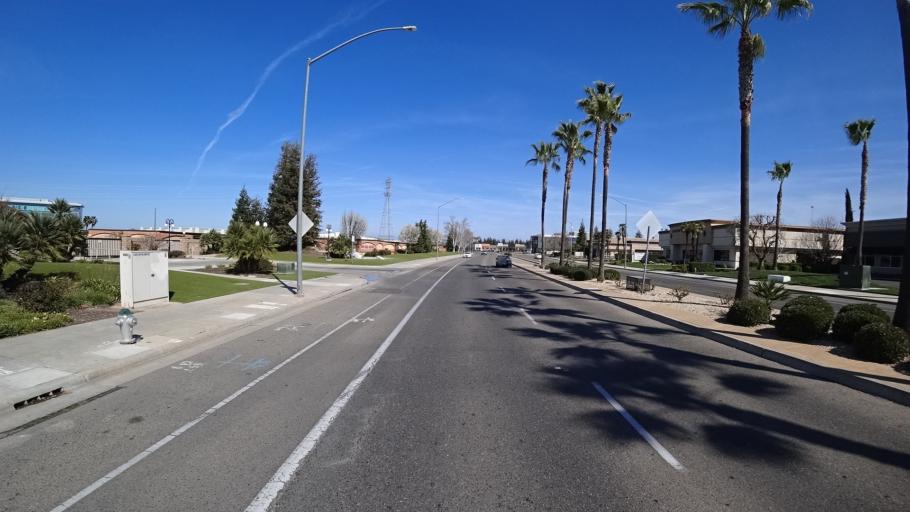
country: US
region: California
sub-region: Fresno County
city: Fresno
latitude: 36.8484
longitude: -119.8074
